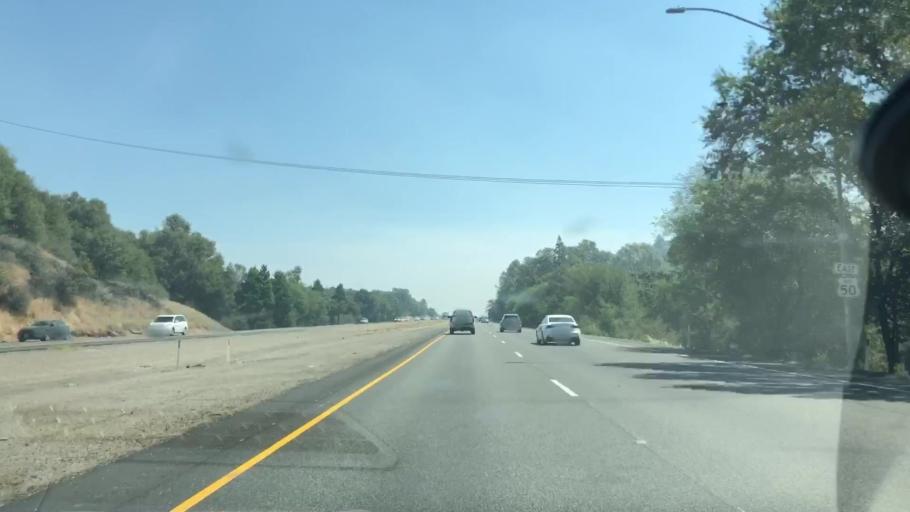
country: US
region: California
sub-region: El Dorado County
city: Deer Park
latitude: 38.7061
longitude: -120.8523
